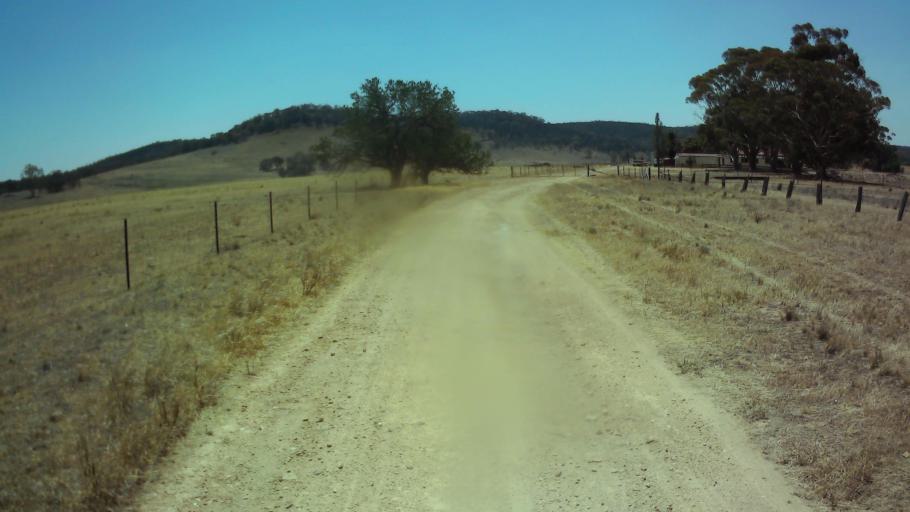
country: AU
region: New South Wales
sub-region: Weddin
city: Grenfell
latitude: -33.9126
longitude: 148.3218
